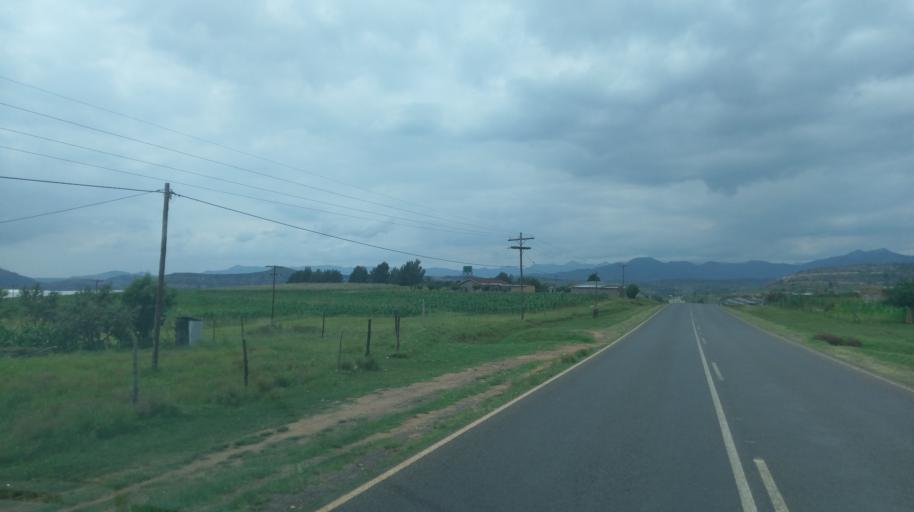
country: LS
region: Leribe
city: Leribe
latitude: -28.9357
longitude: 28.1556
